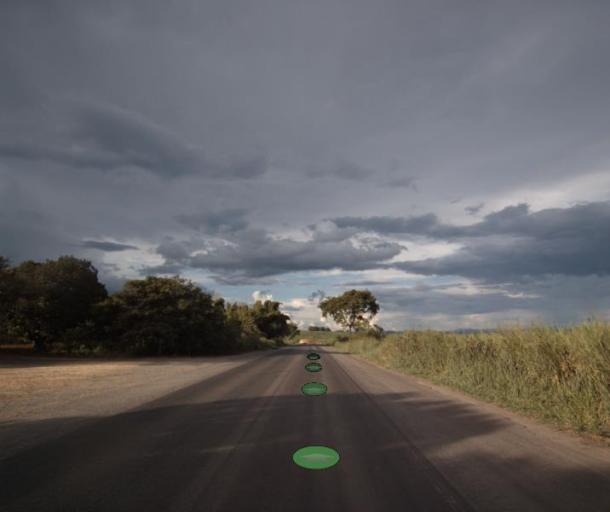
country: BR
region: Goias
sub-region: Itapaci
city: Itapaci
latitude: -15.1082
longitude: -49.4845
